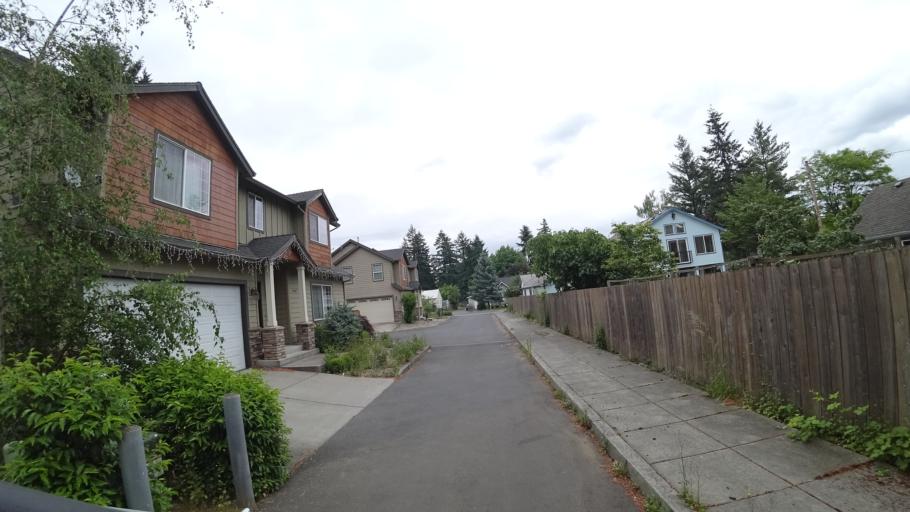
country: US
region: Oregon
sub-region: Multnomah County
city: Lents
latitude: 45.4995
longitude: -122.5462
